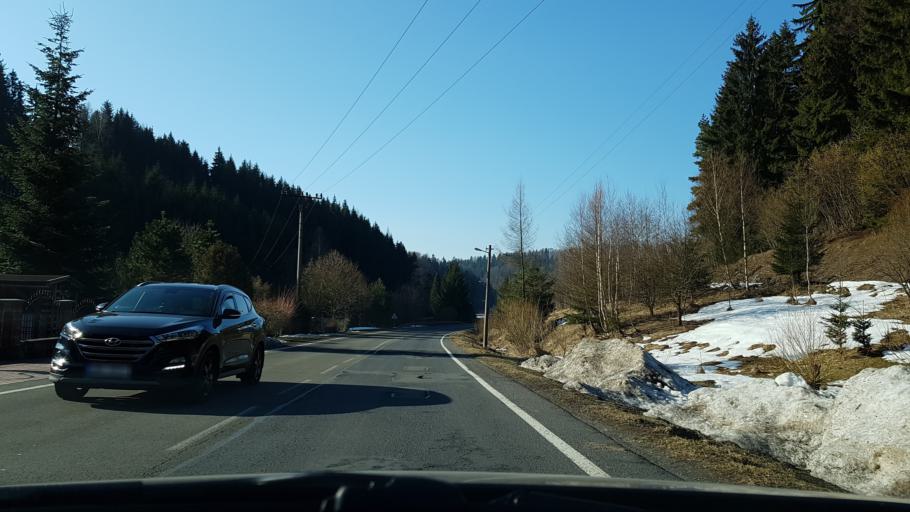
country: CZ
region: Olomoucky
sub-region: Okres Sumperk
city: Hanusovice
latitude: 50.1123
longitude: 17.0046
